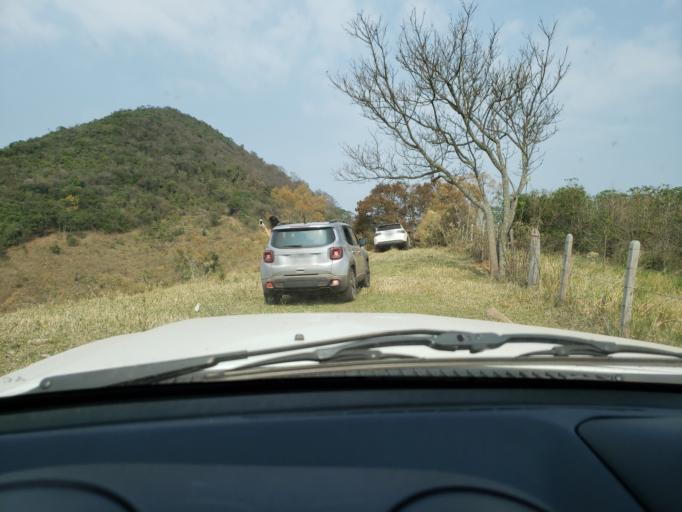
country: BR
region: Minas Gerais
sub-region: Jacutinga
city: Jacutinga
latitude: -22.3444
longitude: -46.5874
